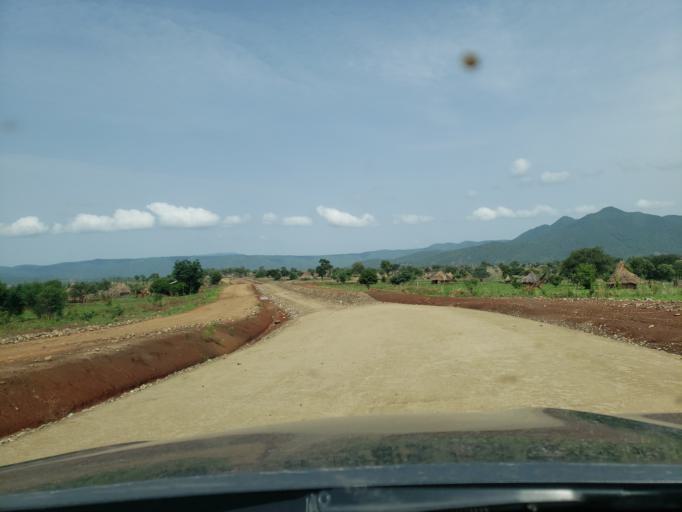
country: ET
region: Oromiya
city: Mendi
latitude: 10.1216
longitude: 35.1495
